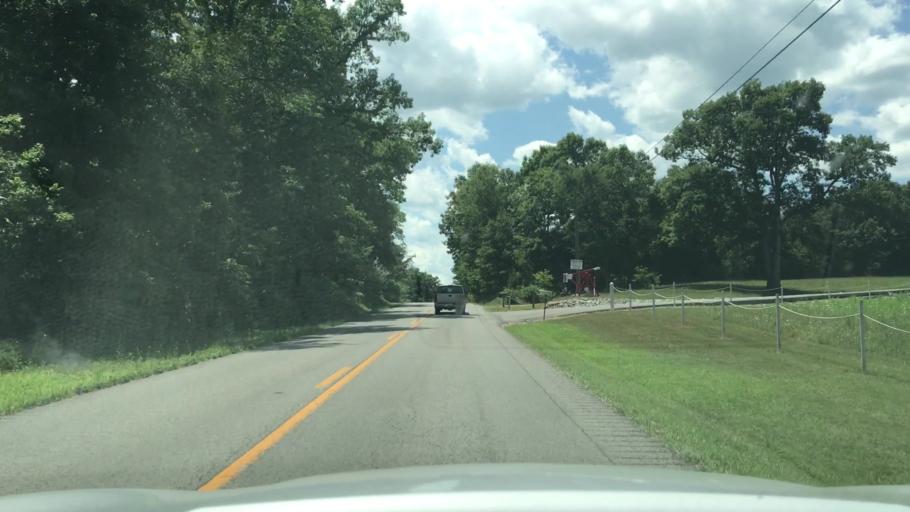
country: US
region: Kentucky
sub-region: Muhlenberg County
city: Greenville
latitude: 37.1836
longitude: -87.2294
